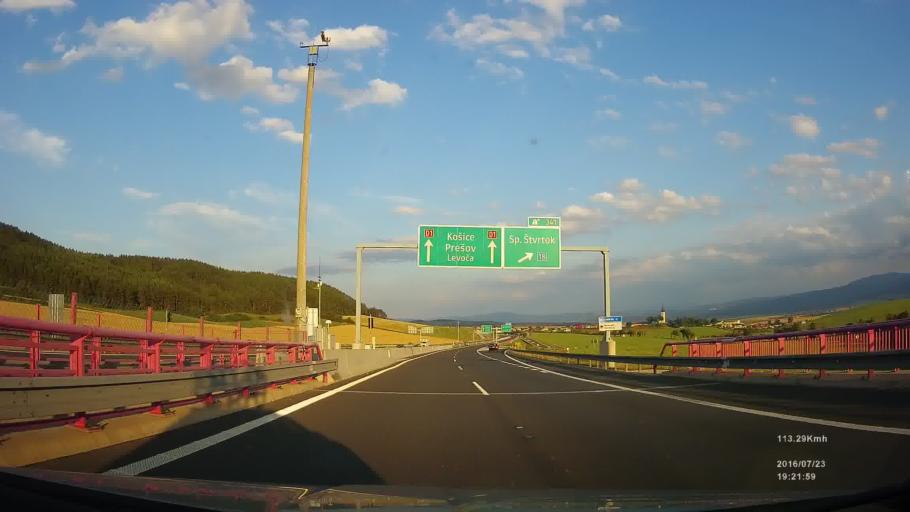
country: SK
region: Presovsky
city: Lubica
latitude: 49.0158
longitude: 20.4503
